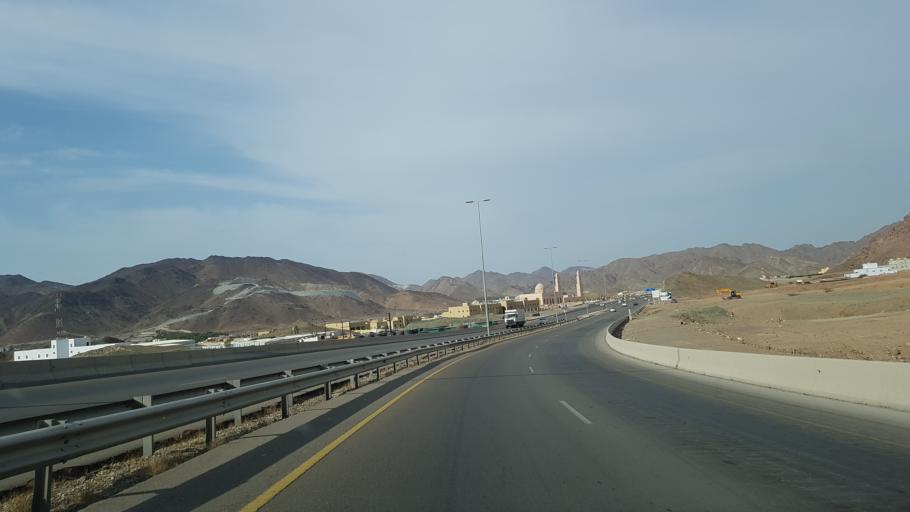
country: OM
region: Muhafazat ad Dakhiliyah
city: Bidbid
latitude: 23.4589
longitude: 58.1171
